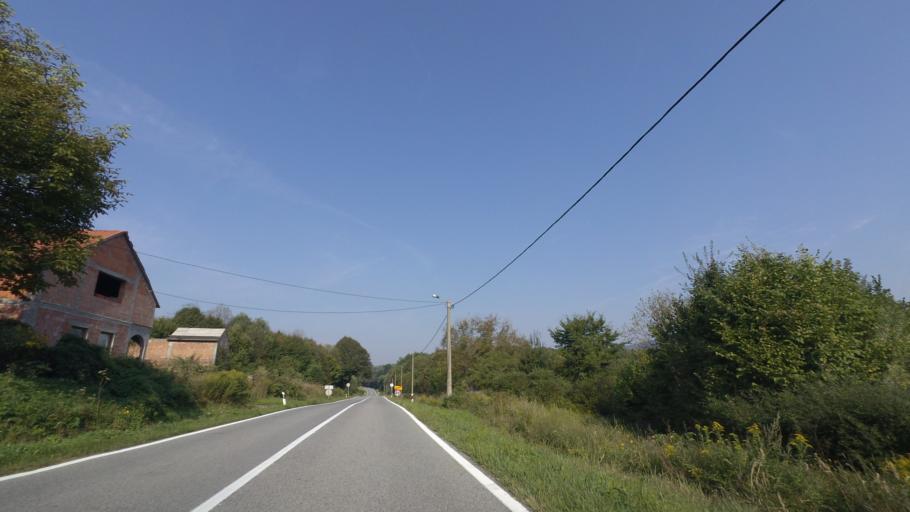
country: HR
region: Bjelovarsko-Bilogorska
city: Sirac
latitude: 45.4684
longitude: 17.3782
